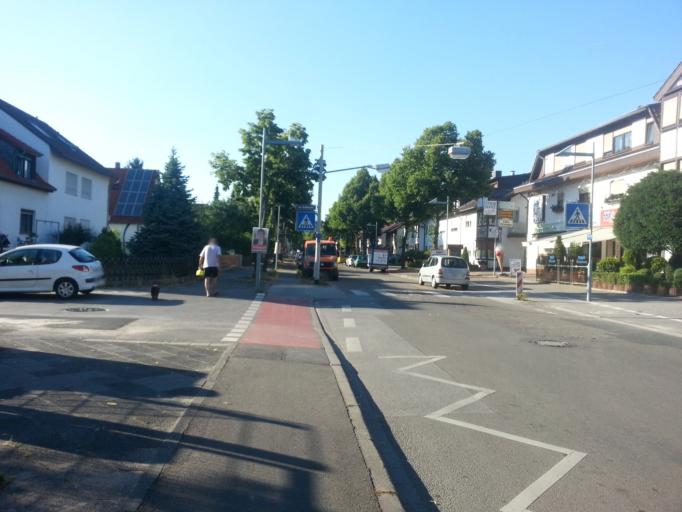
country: DE
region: Baden-Wuerttemberg
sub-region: Karlsruhe Region
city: Mannheim
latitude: 49.5260
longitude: 8.5109
